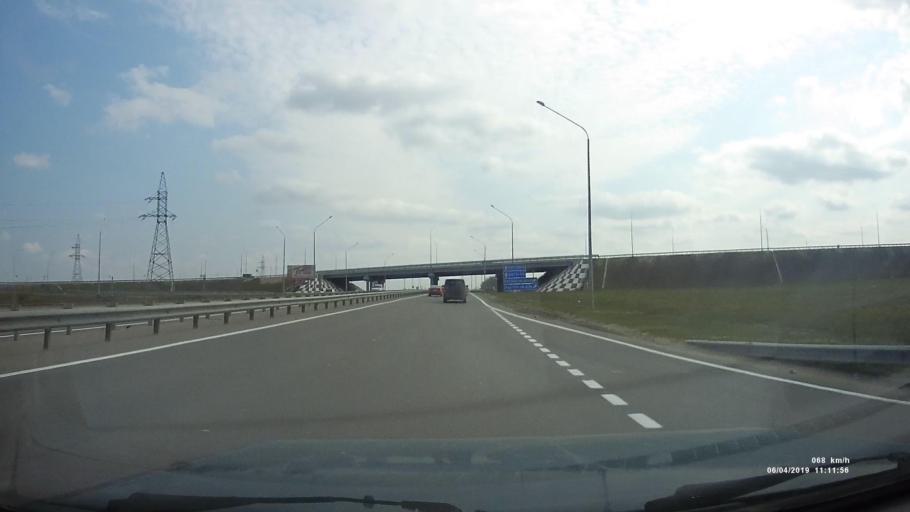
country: RU
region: Rostov
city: Kuleshovka
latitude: 47.0843
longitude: 39.4897
